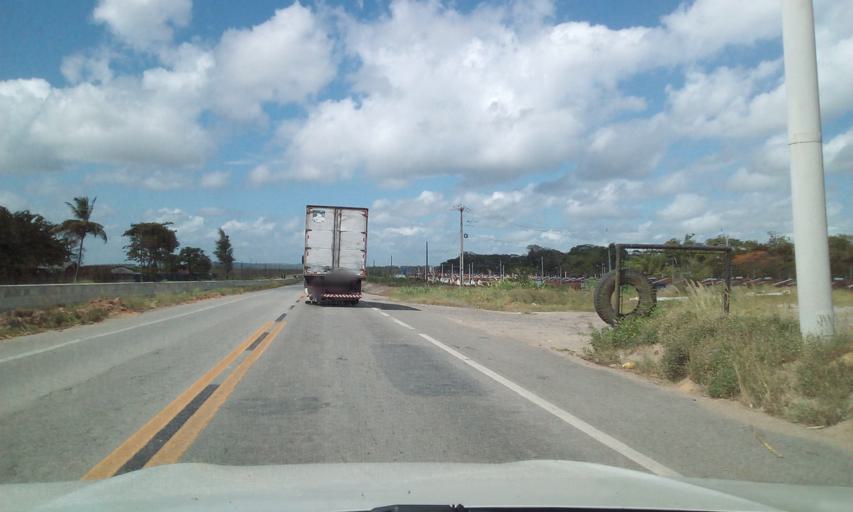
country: BR
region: Alagoas
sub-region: Pilar
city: Pilar
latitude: -9.5598
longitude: -35.9682
